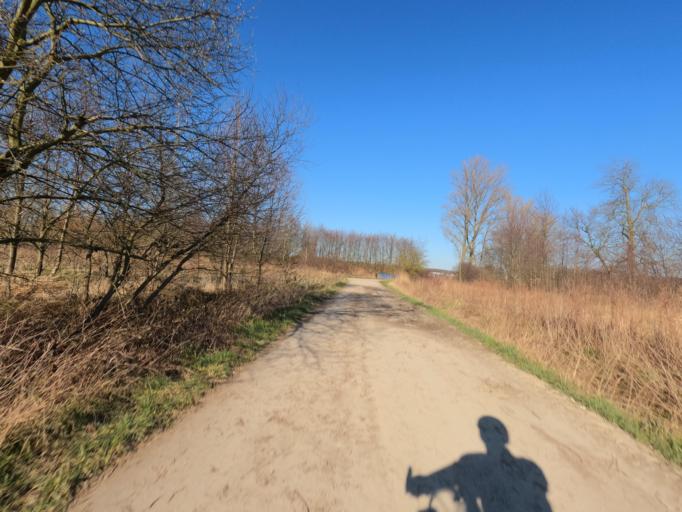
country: DE
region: North Rhine-Westphalia
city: Huckelhoven
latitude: 51.0283
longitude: 6.2547
